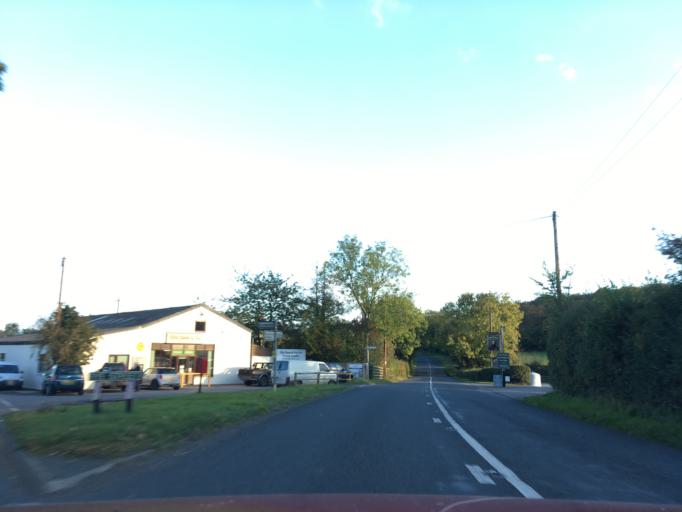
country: GB
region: England
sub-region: Worcestershire
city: Great Malvern
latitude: 52.0177
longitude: -2.3193
